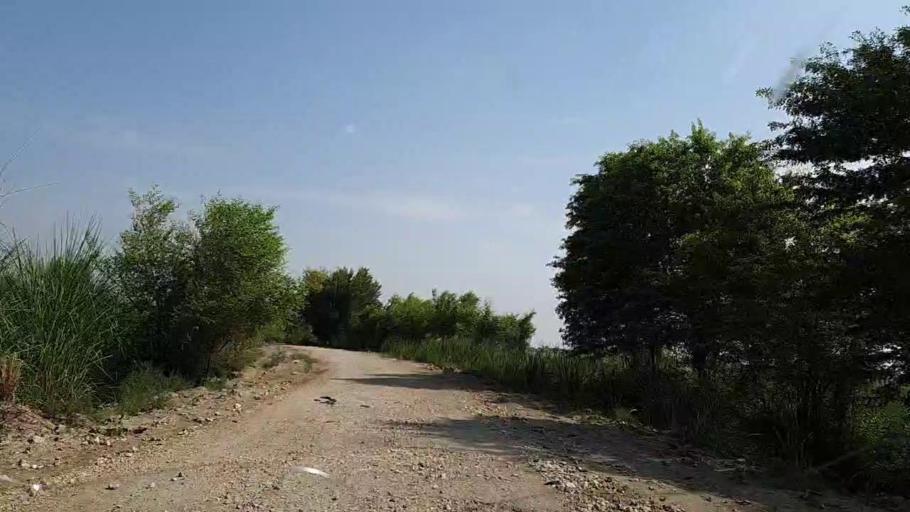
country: PK
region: Sindh
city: Khanpur
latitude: 27.7091
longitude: 69.3621
